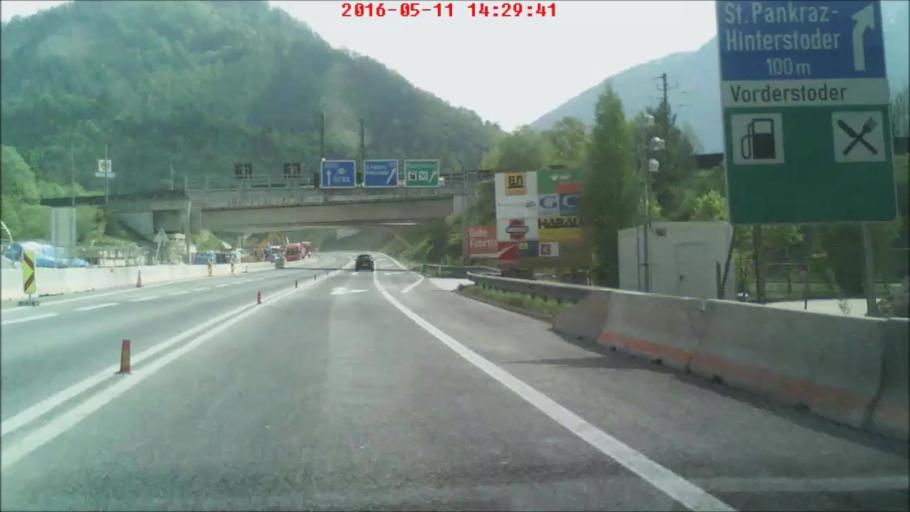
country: AT
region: Upper Austria
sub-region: Politischer Bezirk Kirchdorf an der Krems
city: Micheldorf in Oberoesterreich
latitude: 47.7841
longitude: 14.1738
